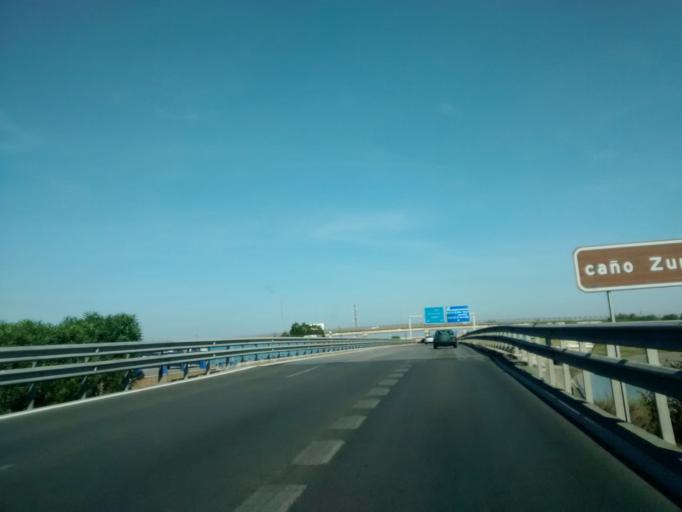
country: ES
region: Andalusia
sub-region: Provincia de Cadiz
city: San Fernando
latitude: 36.4656
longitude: -6.1638
